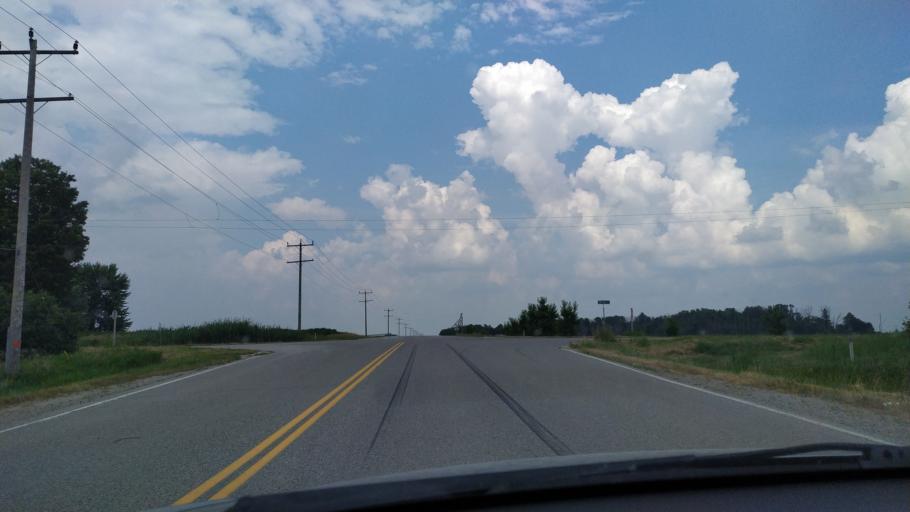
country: CA
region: Ontario
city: London
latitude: 43.1624
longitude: -81.1519
